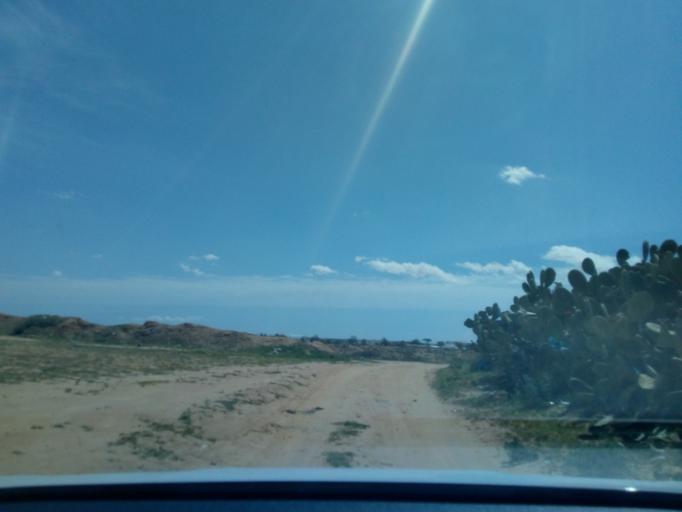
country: TN
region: Safaqis
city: Sfax
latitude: 34.7348
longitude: 10.4996
